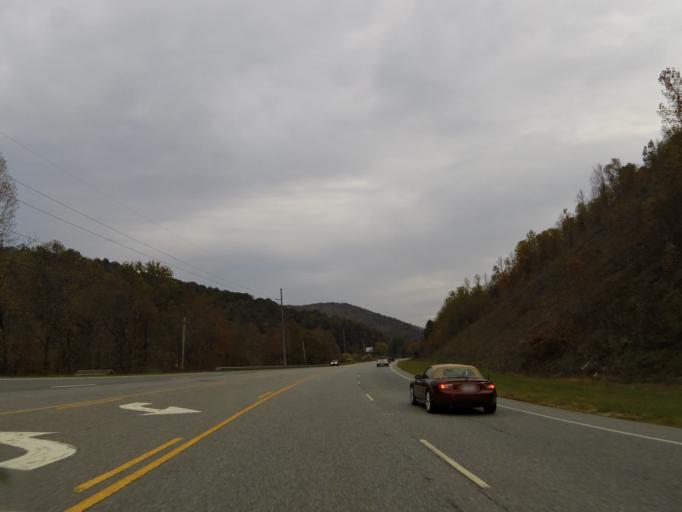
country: US
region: North Carolina
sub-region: Caldwell County
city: Lenoir
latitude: 36.0256
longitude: -81.5790
